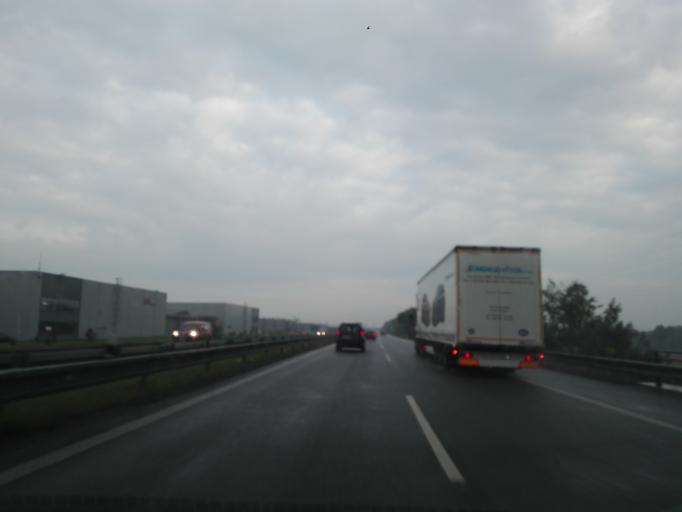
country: CZ
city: Paskov
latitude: 49.7594
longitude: 18.2742
